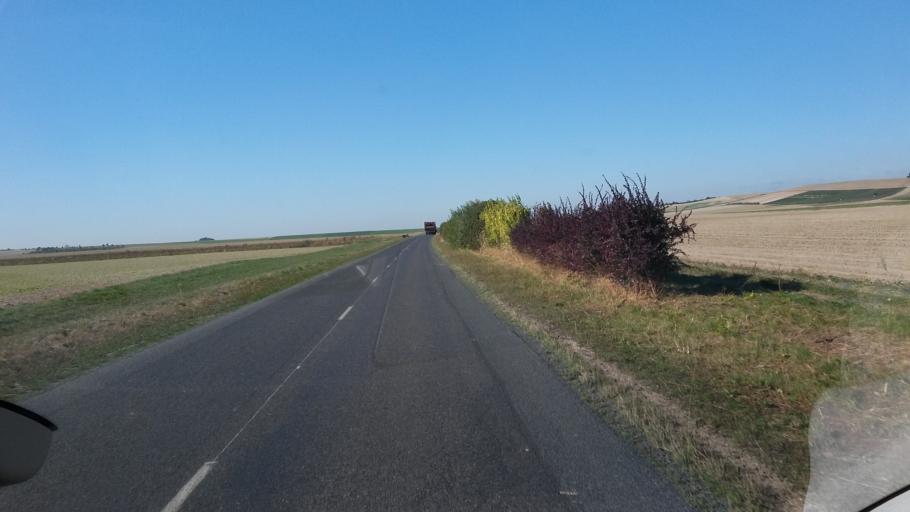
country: FR
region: Champagne-Ardenne
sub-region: Departement de la Marne
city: Connantre
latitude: 48.7471
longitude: 3.8887
